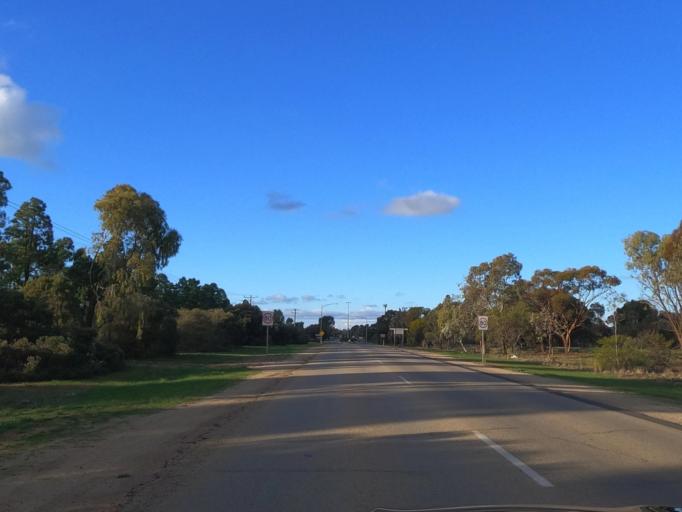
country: AU
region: Victoria
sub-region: Swan Hill
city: Swan Hill
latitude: -35.3439
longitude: 143.5290
